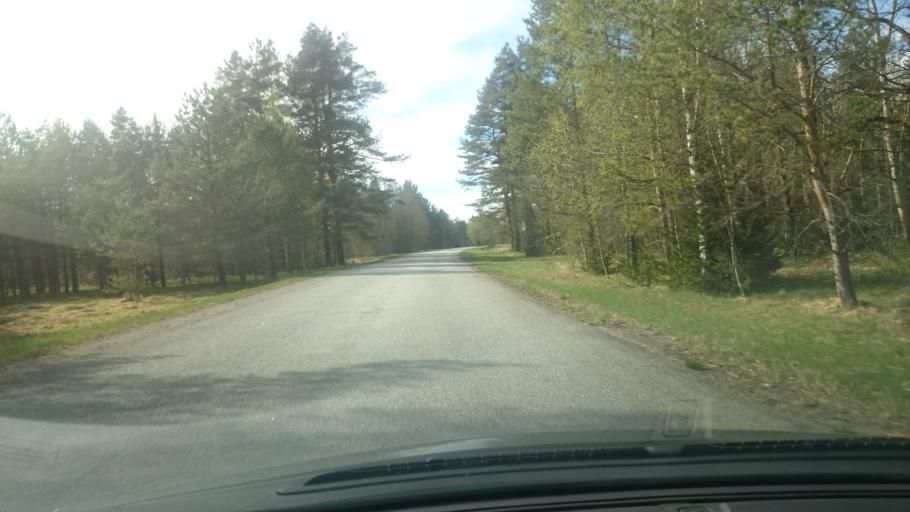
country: EE
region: Ida-Virumaa
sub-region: Sillamaee linn
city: Sillamae
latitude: 59.0847
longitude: 27.6725
